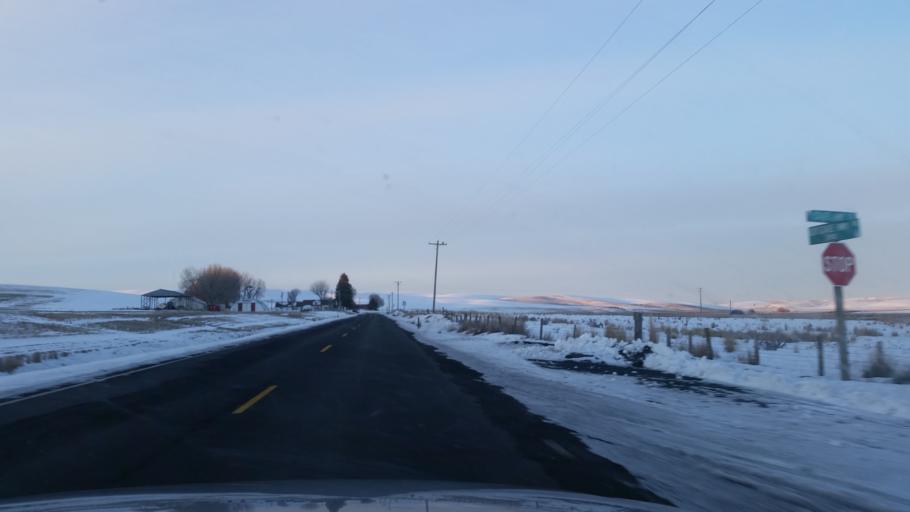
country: US
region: Washington
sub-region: Spokane County
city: Cheney
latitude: 47.1354
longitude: -117.8293
